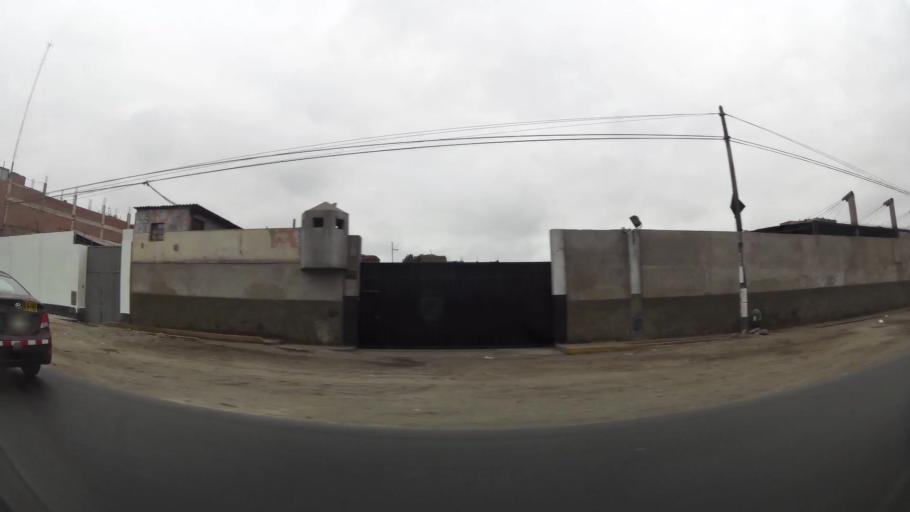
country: PE
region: Lima
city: Lima
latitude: -12.0483
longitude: -77.0608
